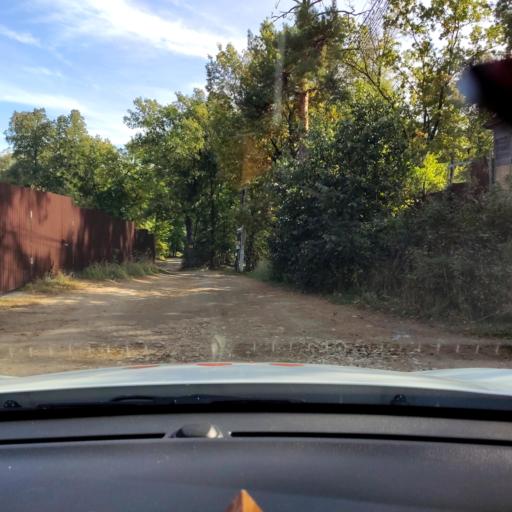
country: RU
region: Tatarstan
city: Staroye Arakchino
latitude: 55.8078
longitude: 49.0129
